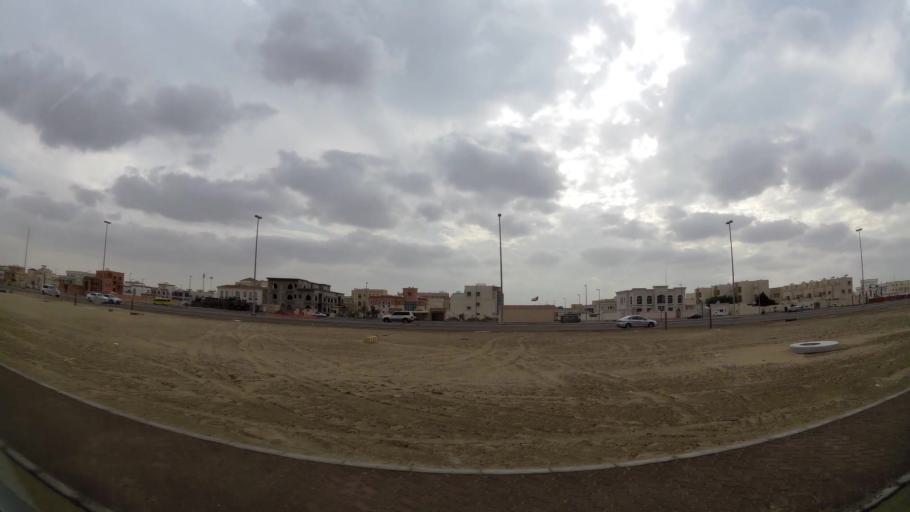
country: AE
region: Abu Dhabi
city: Abu Dhabi
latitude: 24.3481
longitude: 54.6266
